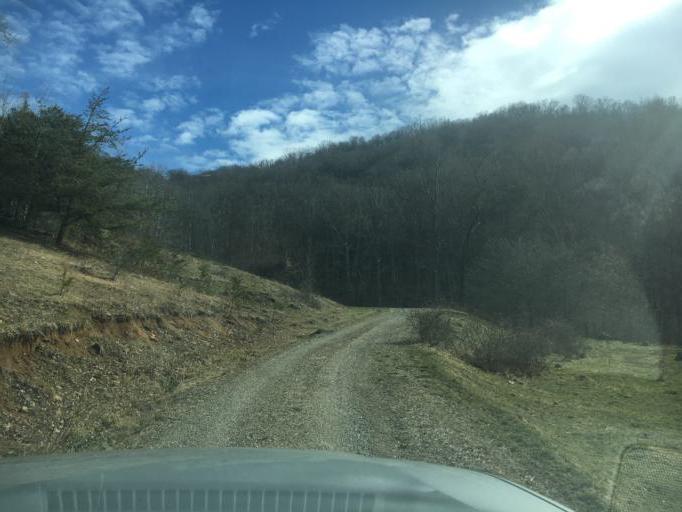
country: US
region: North Carolina
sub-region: Haywood County
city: Canton
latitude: 35.4639
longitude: -82.8371
